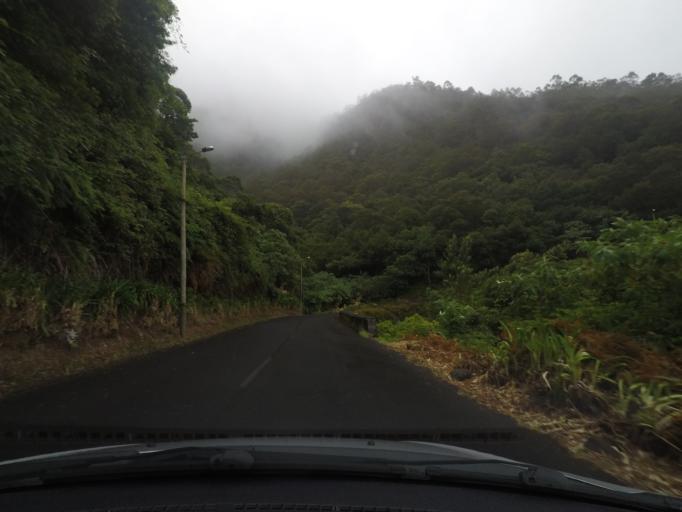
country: PT
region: Madeira
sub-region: Santana
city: Santana
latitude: 32.7847
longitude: -16.8607
